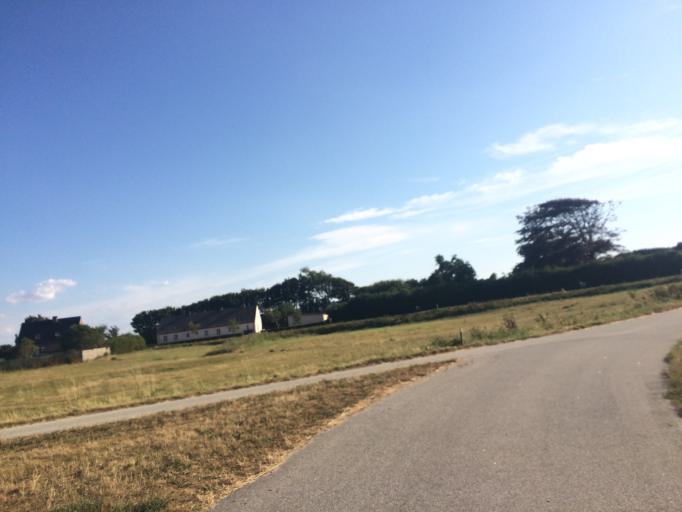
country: DK
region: Central Jutland
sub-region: Holstebro Kommune
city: Vinderup
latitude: 56.6010
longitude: 8.7715
